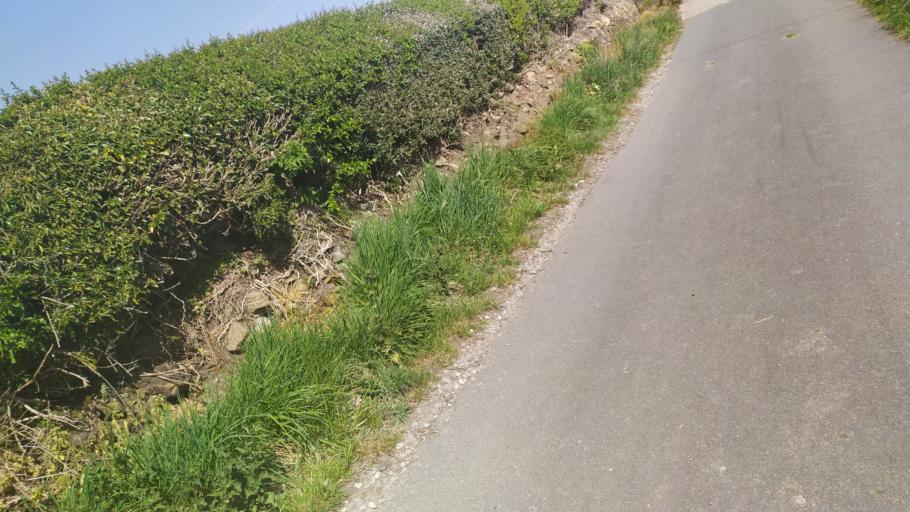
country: GB
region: England
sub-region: City and Borough of Leeds
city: Chapel Allerton
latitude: 53.8769
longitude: -1.5593
